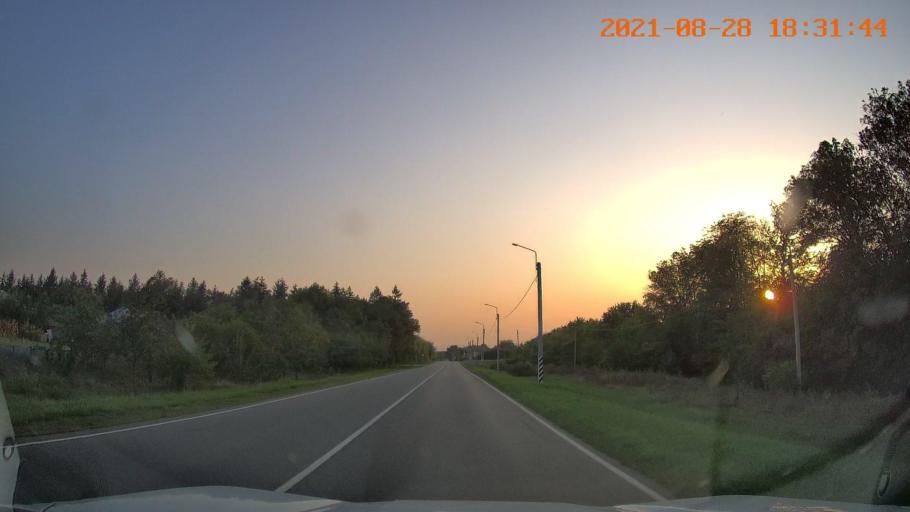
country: RU
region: Adygeya
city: Giaginskaya
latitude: 44.8792
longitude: 40.1990
